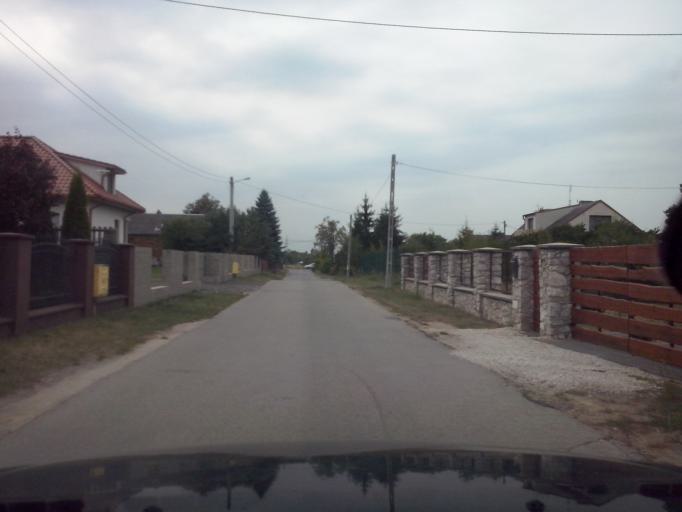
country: PL
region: Swietokrzyskie
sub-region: Powiat kielecki
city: Morawica
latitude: 50.7420
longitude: 20.6181
